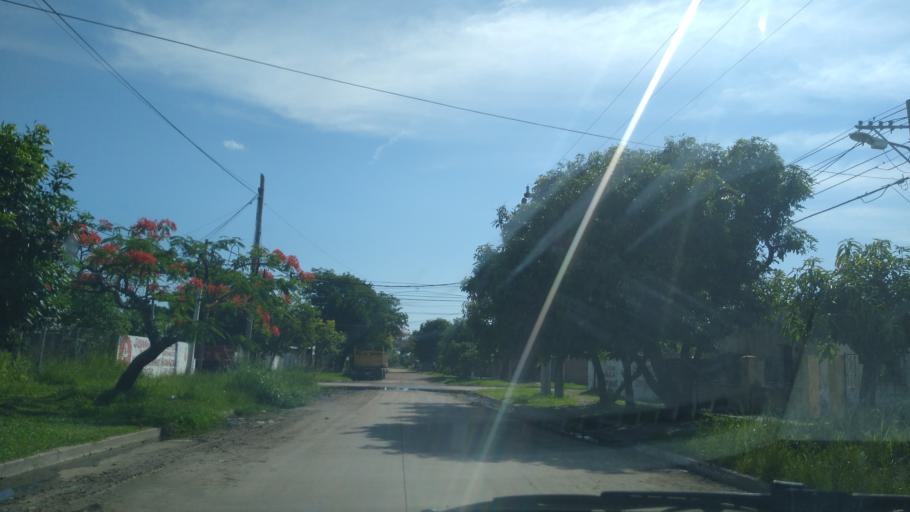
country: AR
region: Chaco
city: Barranqueras
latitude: -27.4860
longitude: -58.9517
